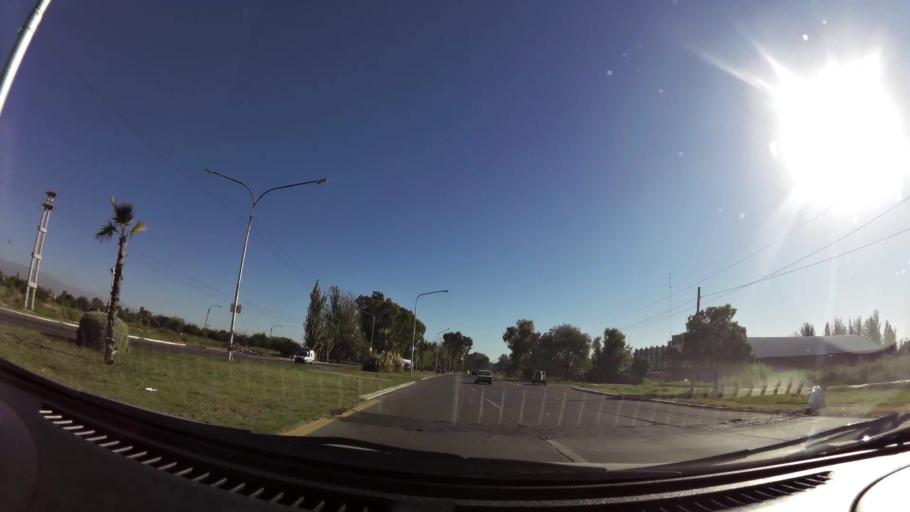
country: AR
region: Mendoza
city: Las Heras
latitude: -32.8511
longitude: -68.8050
